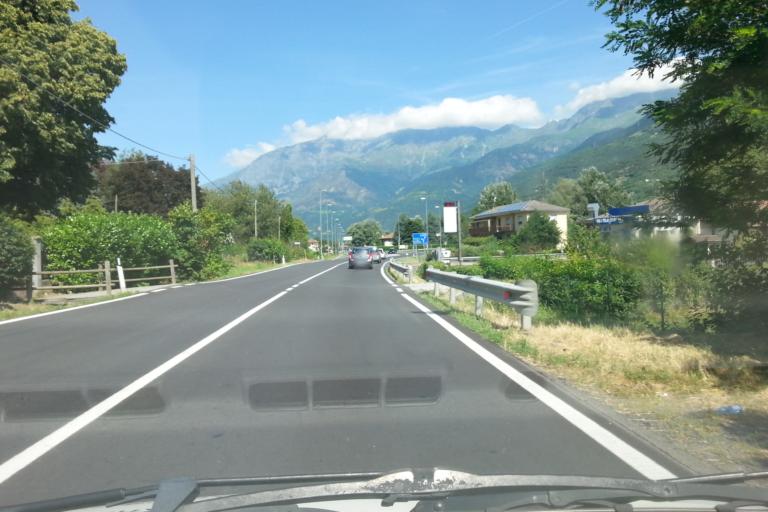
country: IT
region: Piedmont
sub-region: Provincia di Torino
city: Villar Focchiardo
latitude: 45.1153
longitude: 7.2399
